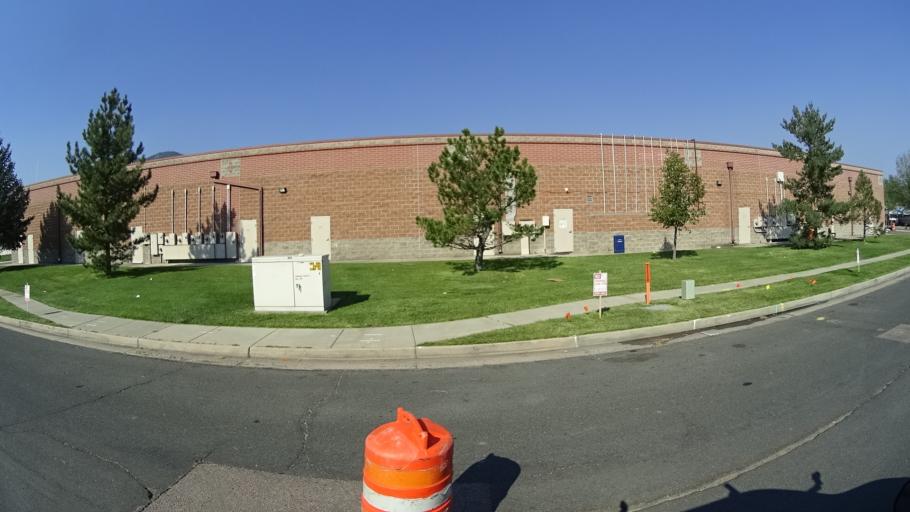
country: US
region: Colorado
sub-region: El Paso County
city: Stratmoor
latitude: 38.7765
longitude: -104.8109
